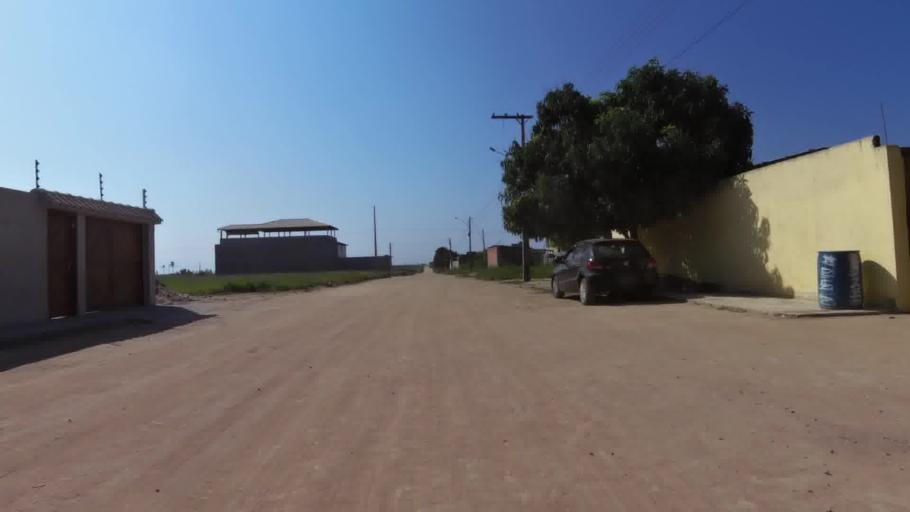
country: BR
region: Espirito Santo
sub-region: Marataizes
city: Marataizes
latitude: -21.0432
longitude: -40.8433
